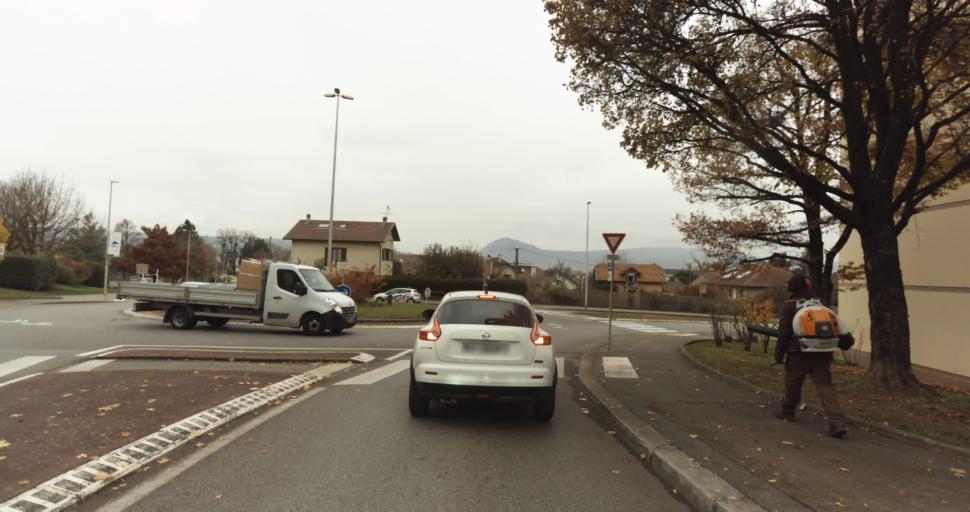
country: FR
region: Rhone-Alpes
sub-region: Departement de la Haute-Savoie
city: Cran-Gevrier
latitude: 45.9046
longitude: 6.0973
